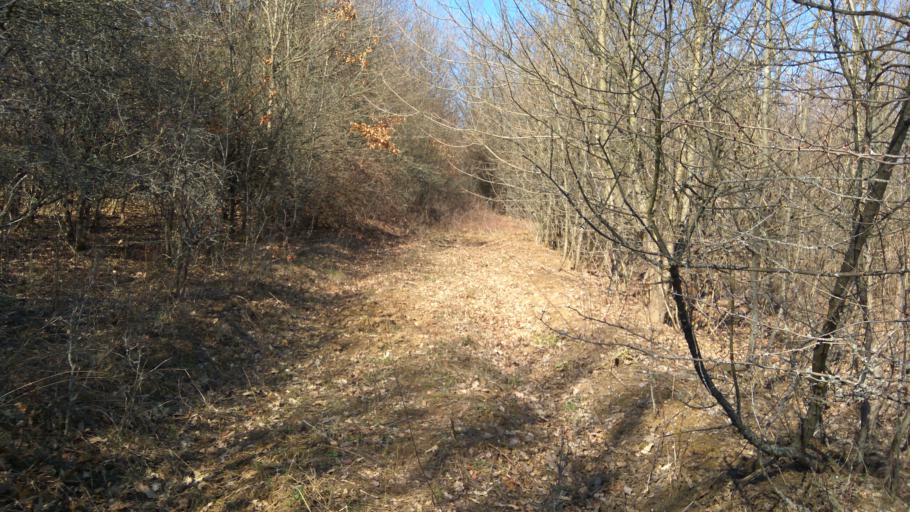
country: HU
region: Pest
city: Csobanka
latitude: 47.6427
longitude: 18.9870
